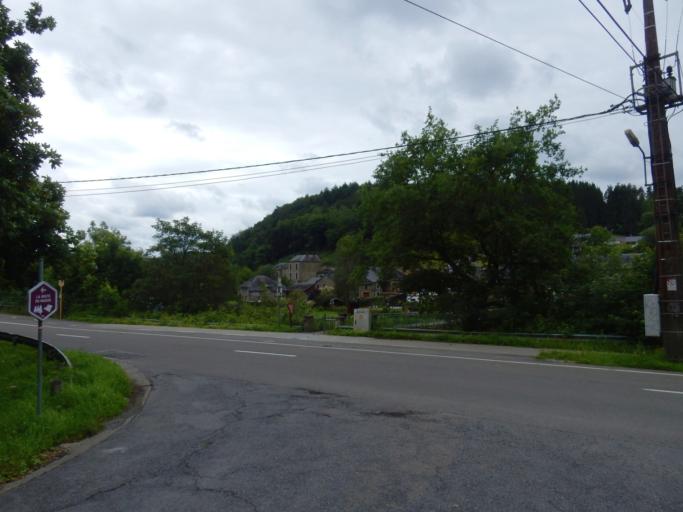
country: BE
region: Wallonia
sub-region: Province de Namur
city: Bievre
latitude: 49.8542
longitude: 4.9679
